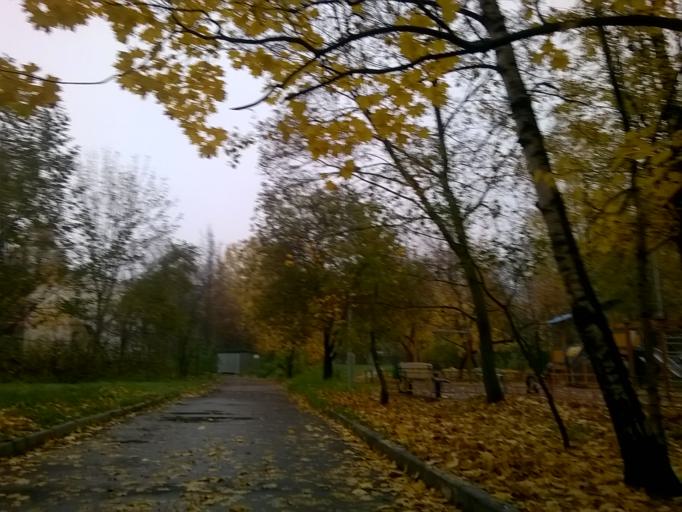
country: RU
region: Moskovskaya
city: Mosrentgen
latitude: 55.6314
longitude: 37.4751
